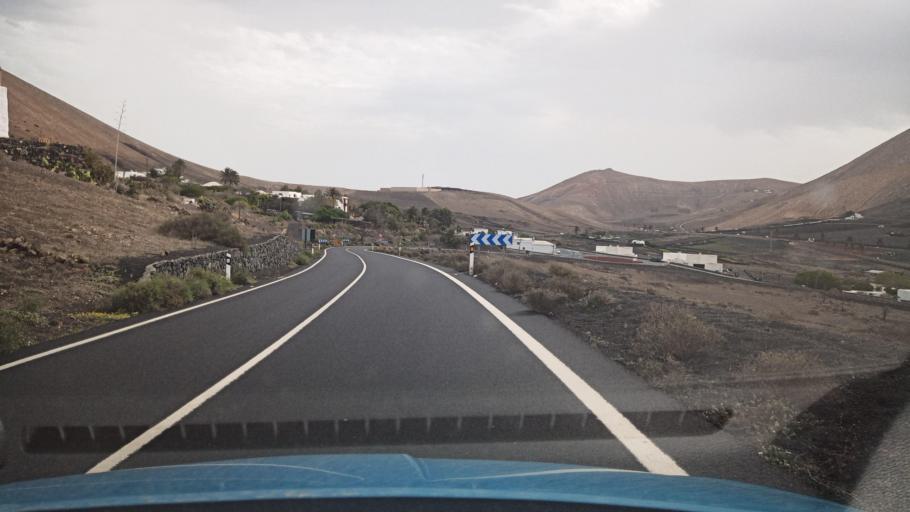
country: ES
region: Canary Islands
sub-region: Provincia de Las Palmas
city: Yaiza
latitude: 28.9501
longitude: -13.7390
